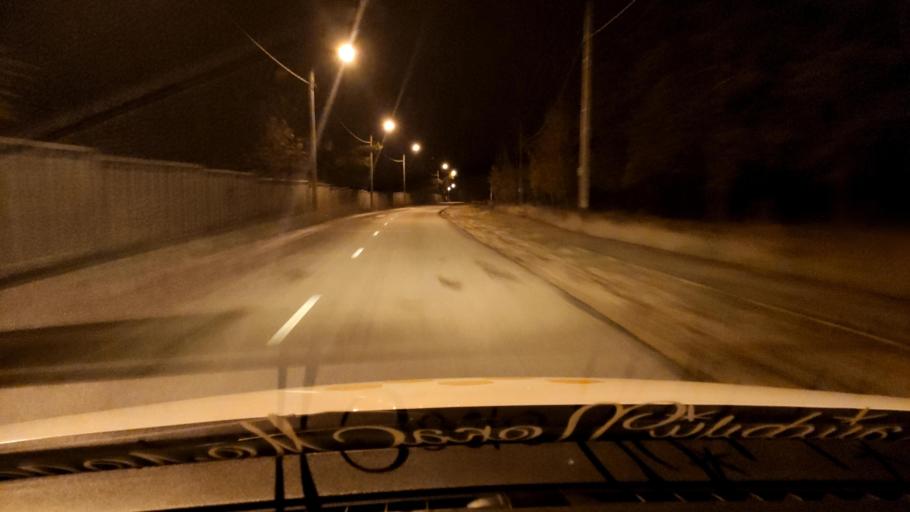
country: RU
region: Voronezj
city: Pridonskoy
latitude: 51.6942
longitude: 39.1042
